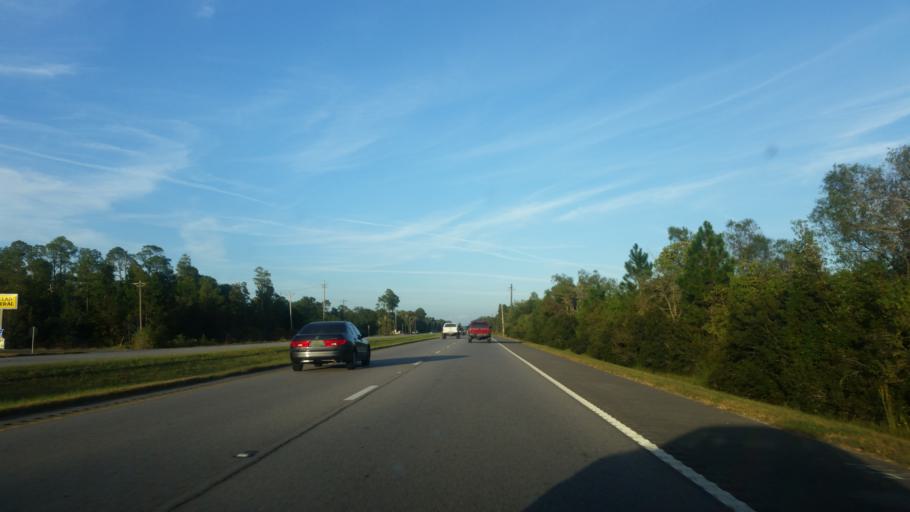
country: US
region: Mississippi
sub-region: Jackson County
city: Moss Point
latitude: 30.4163
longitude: -88.4664
